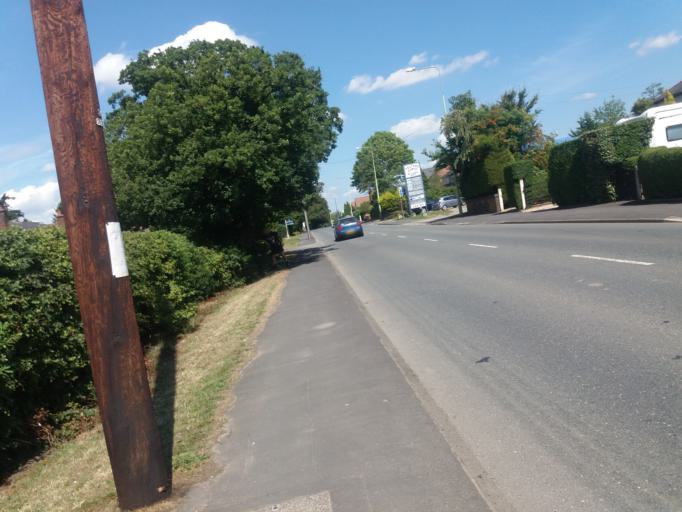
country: GB
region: England
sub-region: Lancashire
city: Euxton
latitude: 53.6733
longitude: -2.6773
